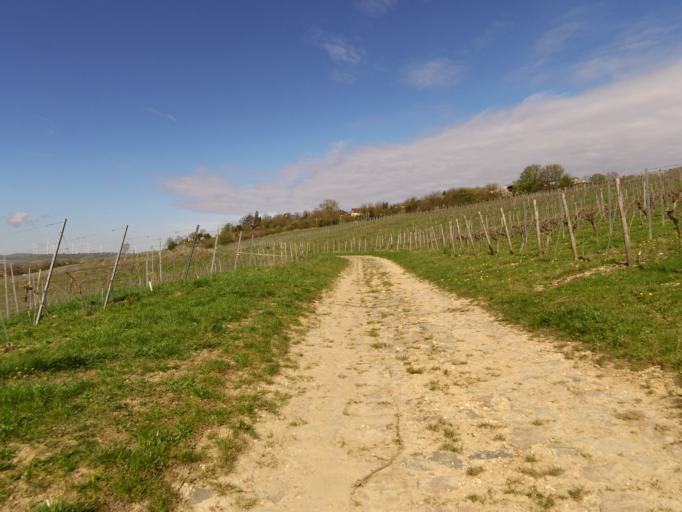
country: DE
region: Rheinland-Pfalz
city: Molsheim
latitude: 49.6465
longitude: 8.1470
